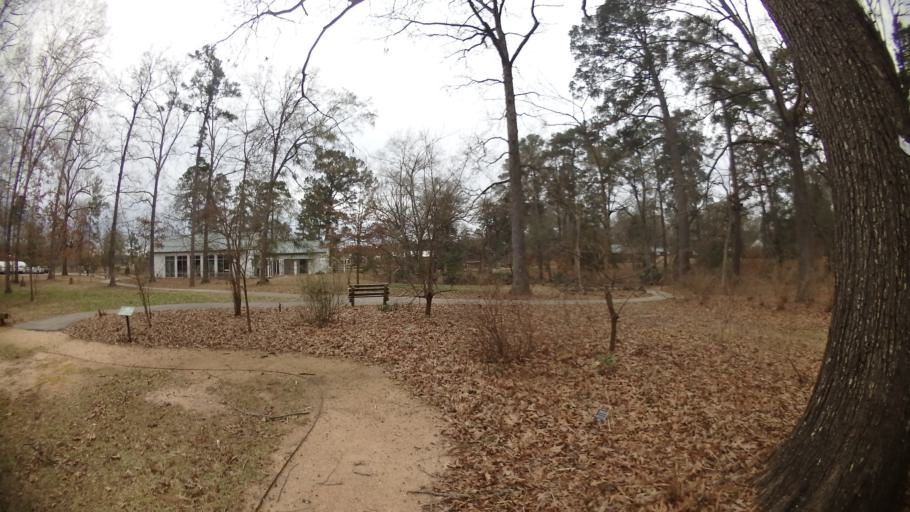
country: US
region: Texas
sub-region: Nacogdoches County
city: Nacogdoches
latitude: 31.6291
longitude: -94.6472
